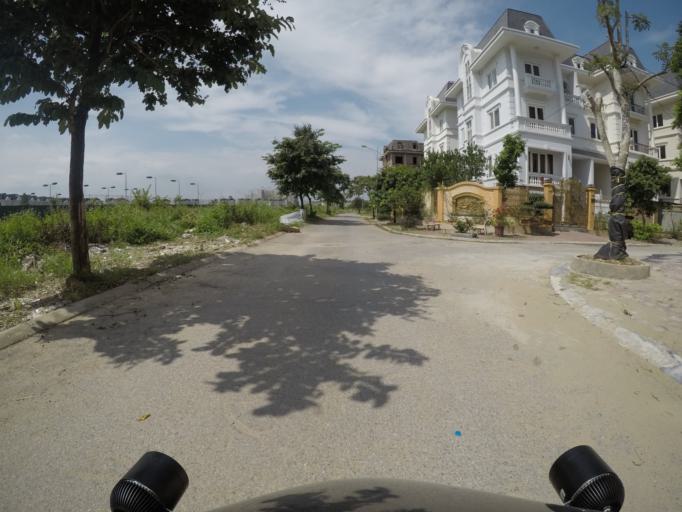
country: VN
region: Ha Noi
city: Troi
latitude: 21.0710
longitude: 105.7141
